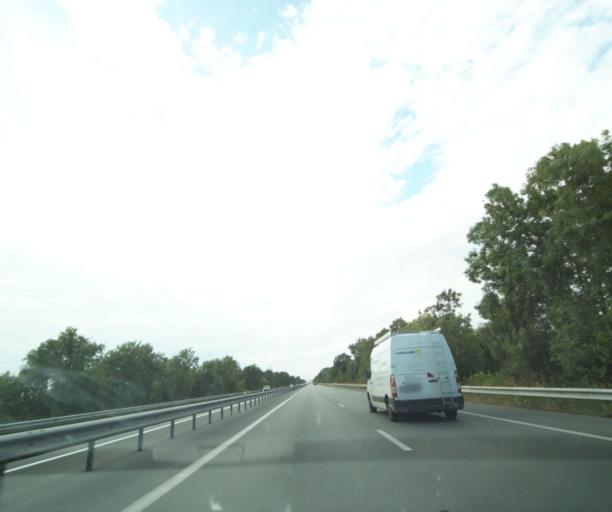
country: FR
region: Poitou-Charentes
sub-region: Departement de la Charente-Maritime
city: Chatelaillon-Plage
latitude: 46.0893
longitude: -1.0834
